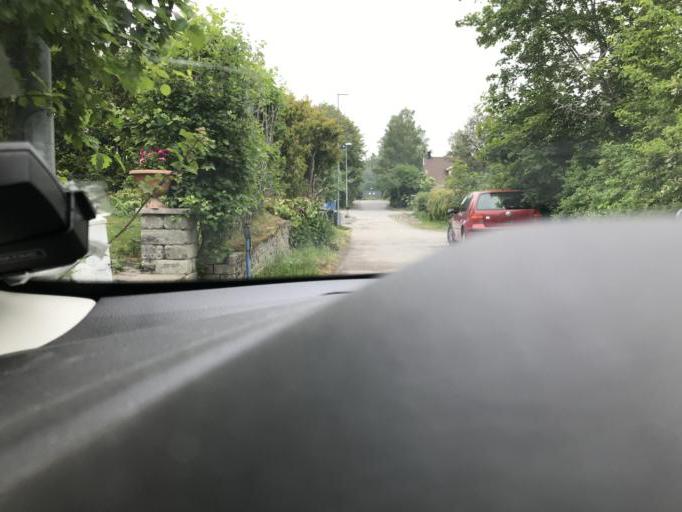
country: SE
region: Stockholm
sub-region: Botkyrka Kommun
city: Tumba
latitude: 59.2098
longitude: 17.8183
